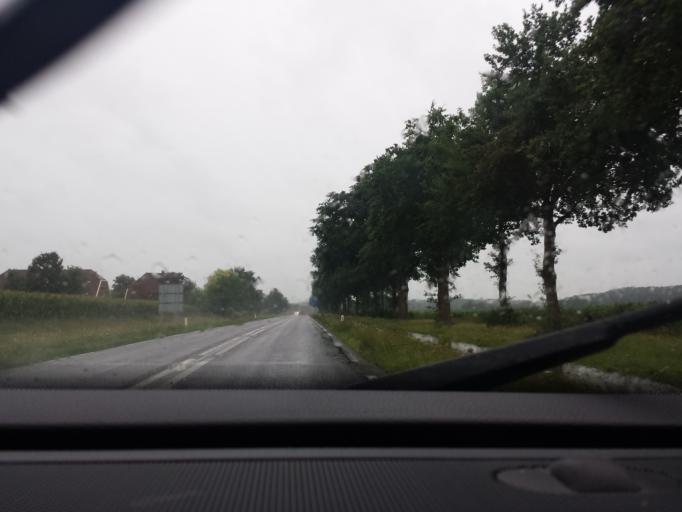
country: NL
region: Gelderland
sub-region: Gemeente Montferland
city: s-Heerenberg
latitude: 51.9200
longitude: 6.2680
